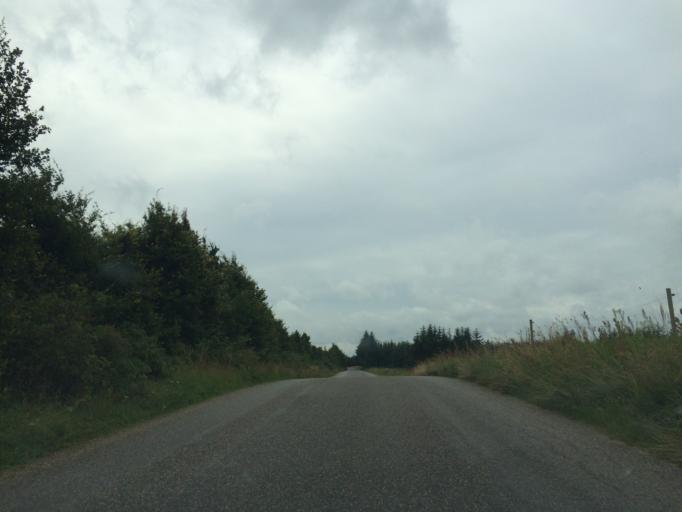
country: DK
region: Central Jutland
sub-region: Silkeborg Kommune
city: Svejbaek
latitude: 56.2424
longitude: 9.6776
